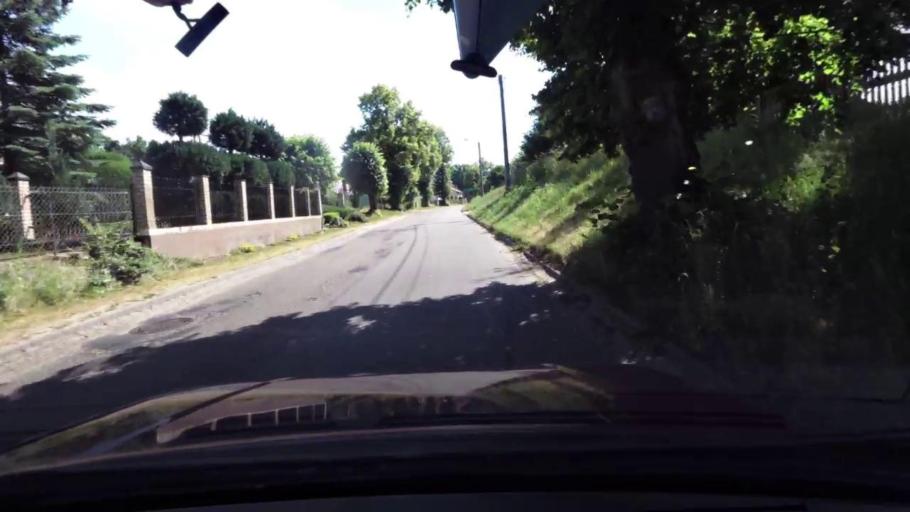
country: PL
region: Pomeranian Voivodeship
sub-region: Powiat slupski
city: Kobylnica
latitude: 54.3501
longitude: 16.9675
